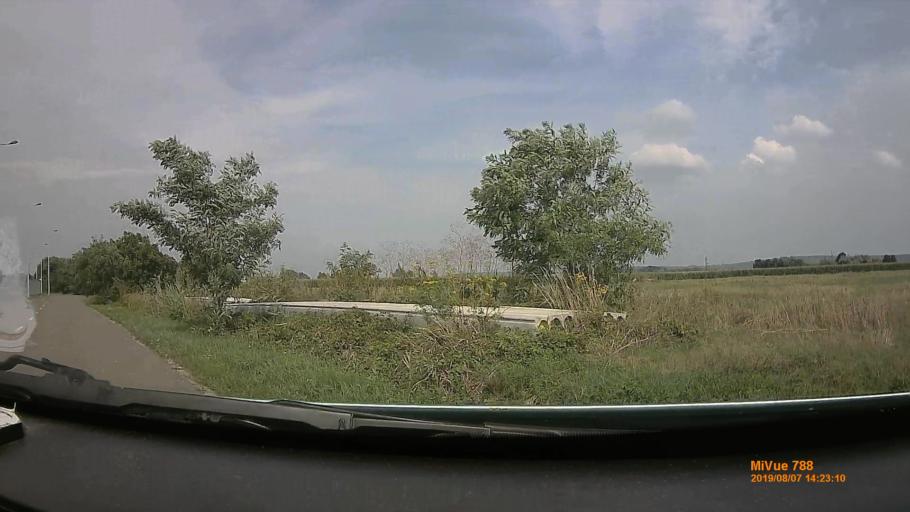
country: HU
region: Borsod-Abauj-Zemplen
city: Szikszo
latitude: 48.1721
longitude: 20.9233
